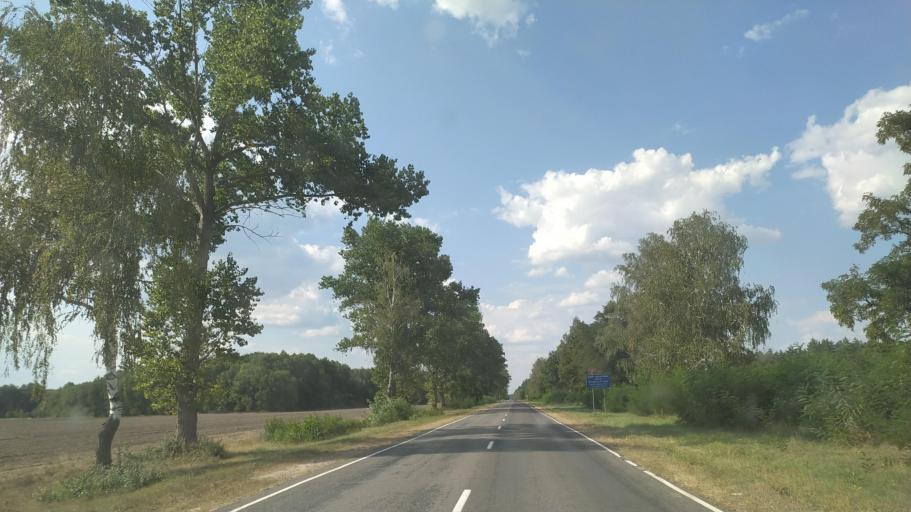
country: BY
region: Brest
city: Drahichyn
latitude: 52.2083
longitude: 25.1401
